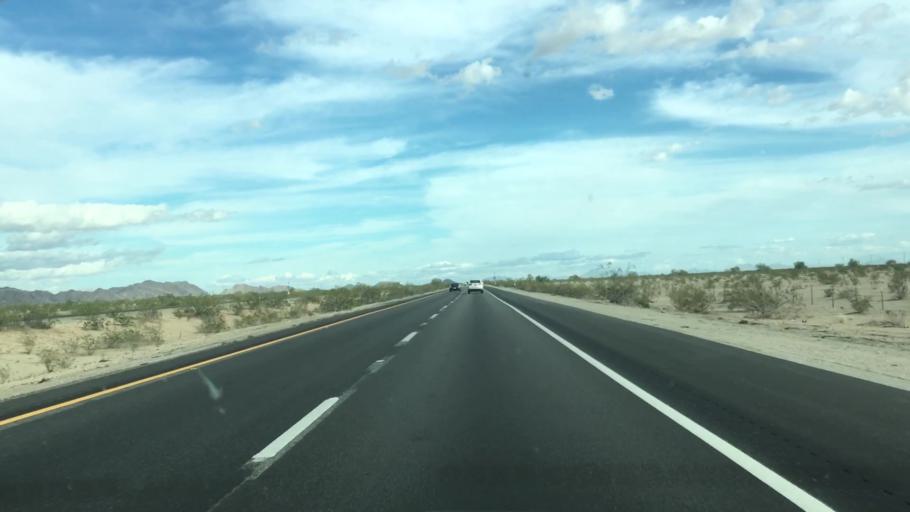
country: US
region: California
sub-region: Riverside County
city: Mesa Verde
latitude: 33.6092
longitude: -114.8530
